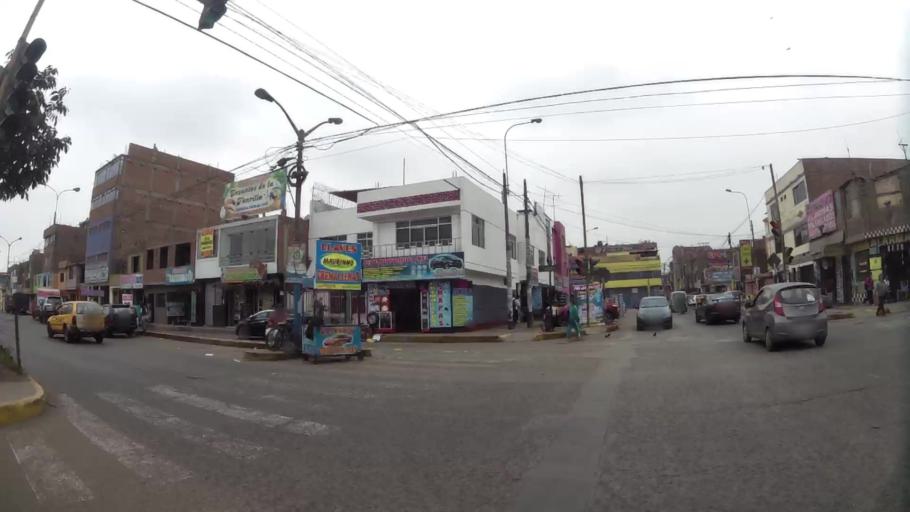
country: PE
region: Lima
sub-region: Lima
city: Independencia
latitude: -11.9836
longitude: -77.0612
